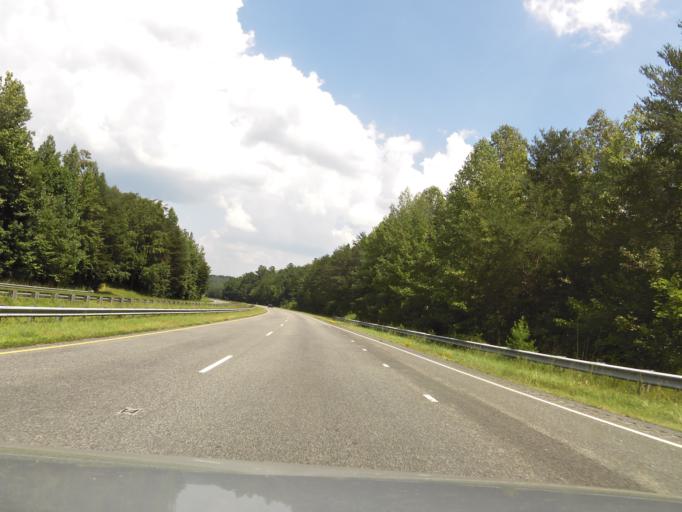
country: US
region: North Carolina
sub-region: Polk County
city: Columbus
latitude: 35.2606
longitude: -82.1773
